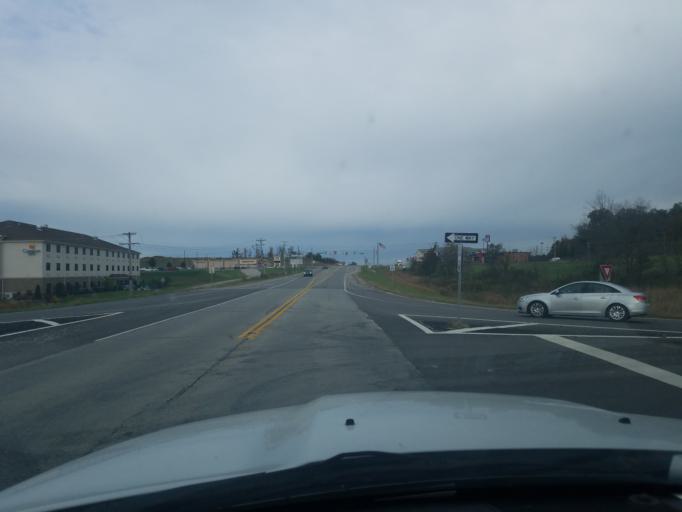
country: US
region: Indiana
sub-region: Dubois County
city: Ferdinand
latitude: 38.2068
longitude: -86.8658
